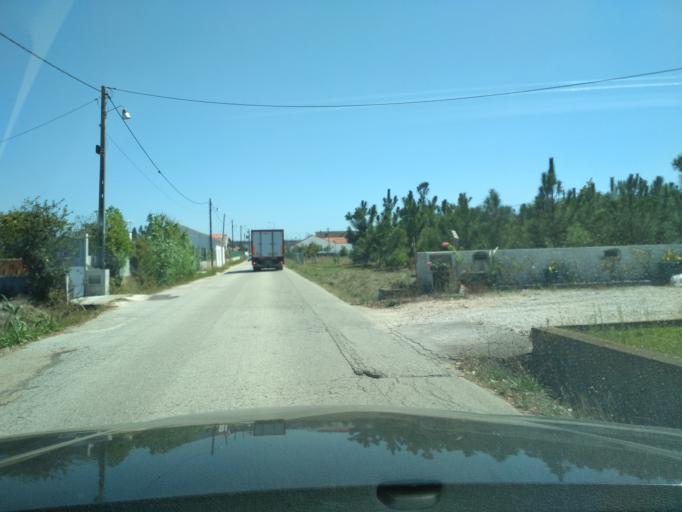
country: PT
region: Coimbra
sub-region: Figueira da Foz
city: Lavos
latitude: 40.0530
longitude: -8.8678
